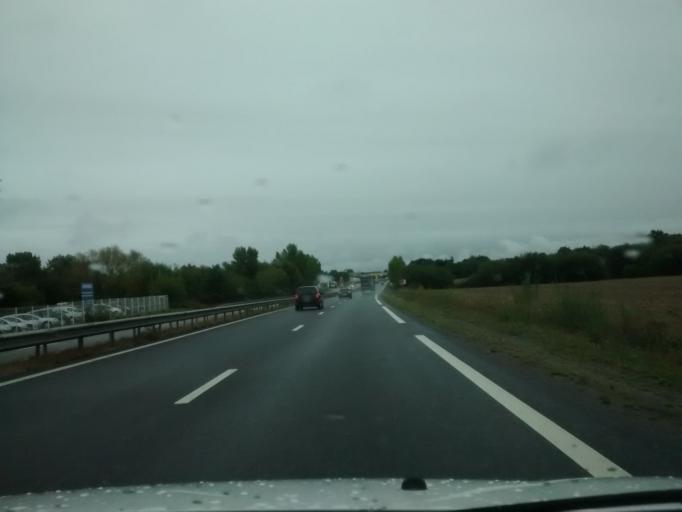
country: FR
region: Brittany
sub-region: Departement d'Ille-et-Vilaine
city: Vern-sur-Seiche
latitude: 48.0576
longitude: -1.6130
